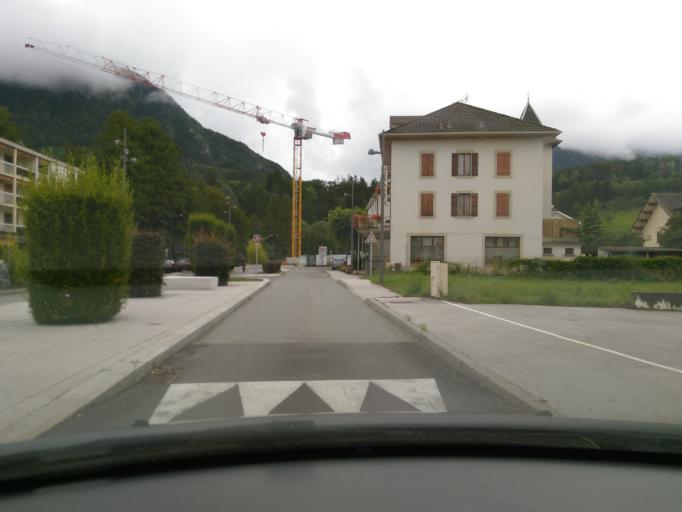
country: FR
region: Rhone-Alpes
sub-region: Departement de la Haute-Savoie
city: Bonneville
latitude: 46.0580
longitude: 6.3748
